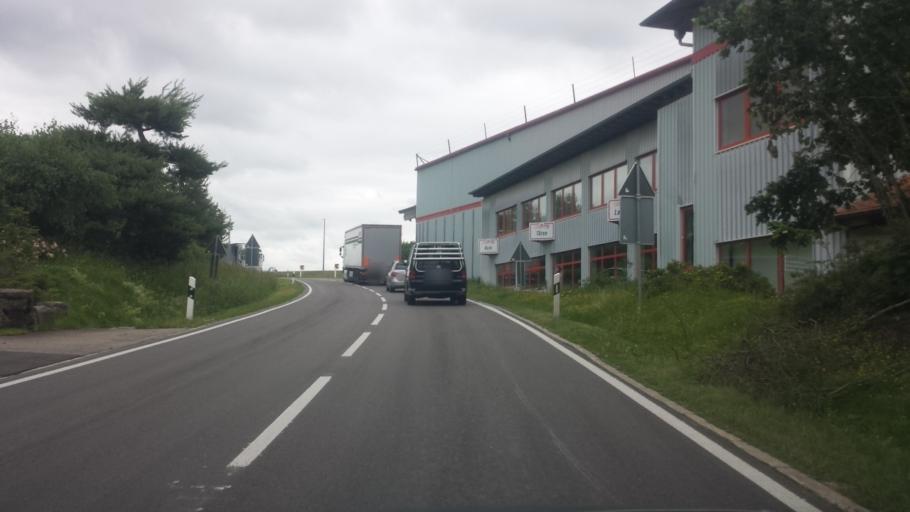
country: DE
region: Baden-Wuerttemberg
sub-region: Regierungsbezirk Stuttgart
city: Rot am See
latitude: 49.2603
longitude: 10.0149
